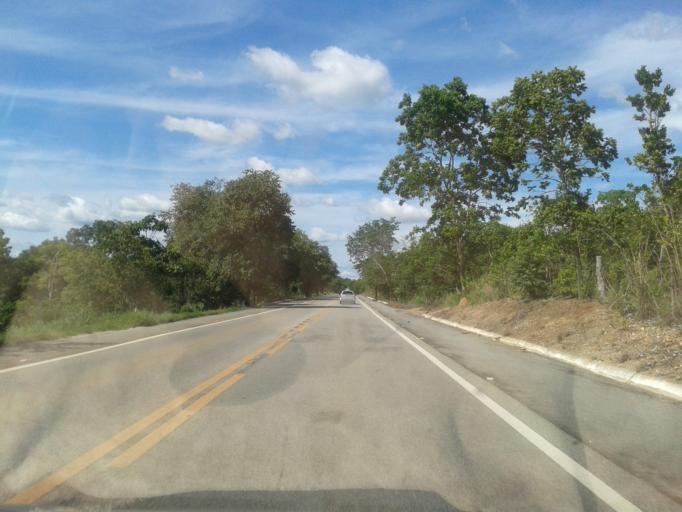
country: BR
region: Goias
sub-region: Itapuranga
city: Itapuranga
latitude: -15.3839
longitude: -50.3900
